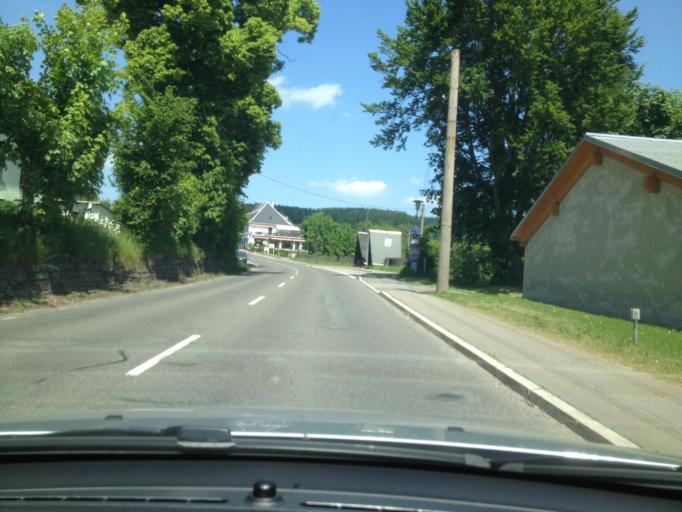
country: DE
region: Saxony
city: Ehrenfriedersdorf
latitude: 50.6198
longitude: 12.9809
